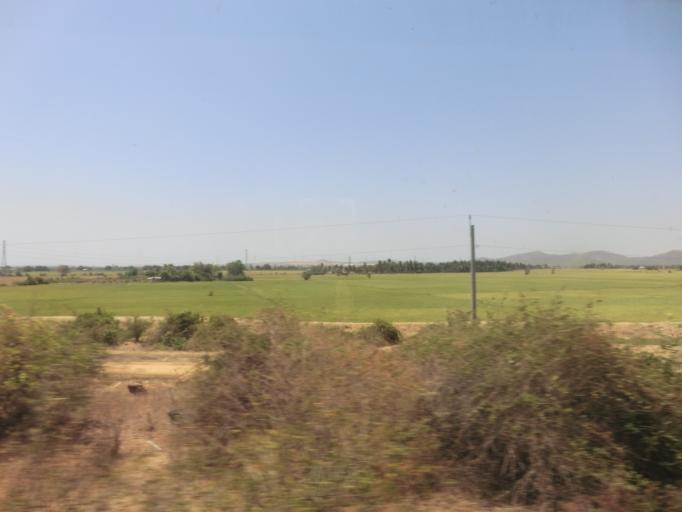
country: VN
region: Binh Thuan
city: Lien Huong
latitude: 11.2735
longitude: 108.7101
